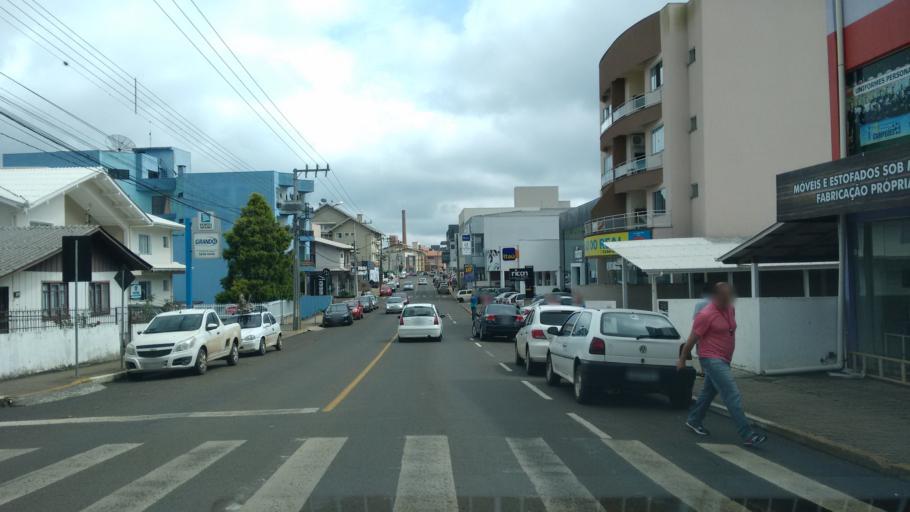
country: BR
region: Santa Catarina
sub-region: Videira
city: Videira
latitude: -27.0275
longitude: -50.9212
